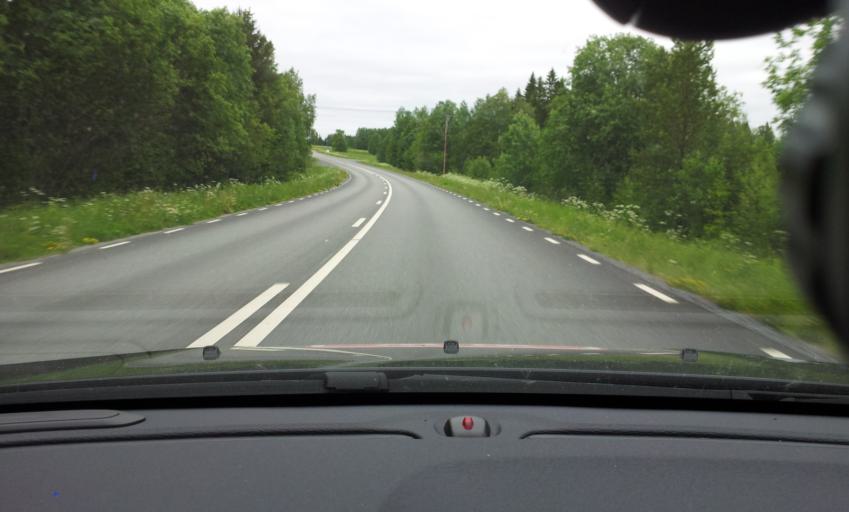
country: SE
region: Jaemtland
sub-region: Krokoms Kommun
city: Krokom
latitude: 63.1228
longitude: 14.2940
